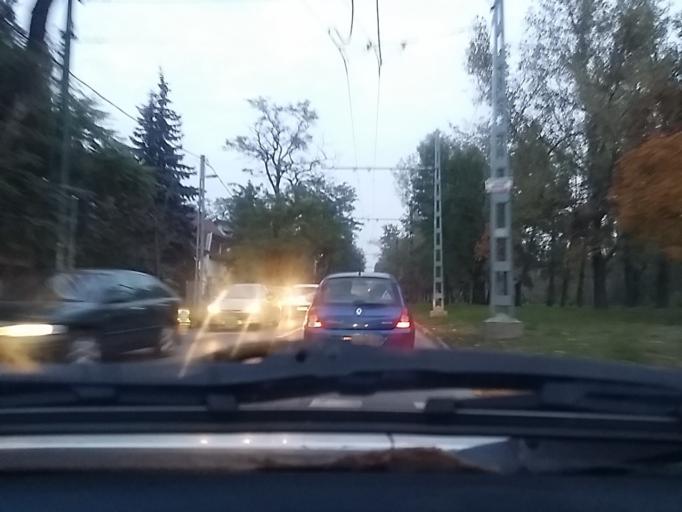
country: HU
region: Budapest
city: Budapest XIV. keruelet
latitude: 47.5225
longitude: 19.1306
